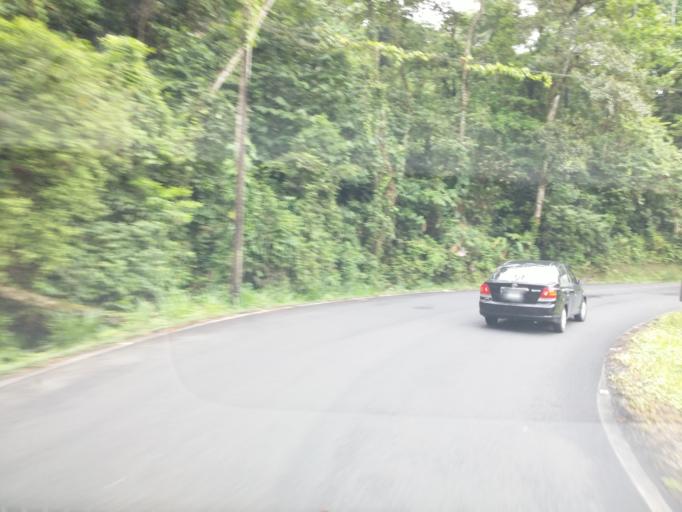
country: CR
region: Alajuela
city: San Ramon
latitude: 10.2208
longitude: -84.5415
